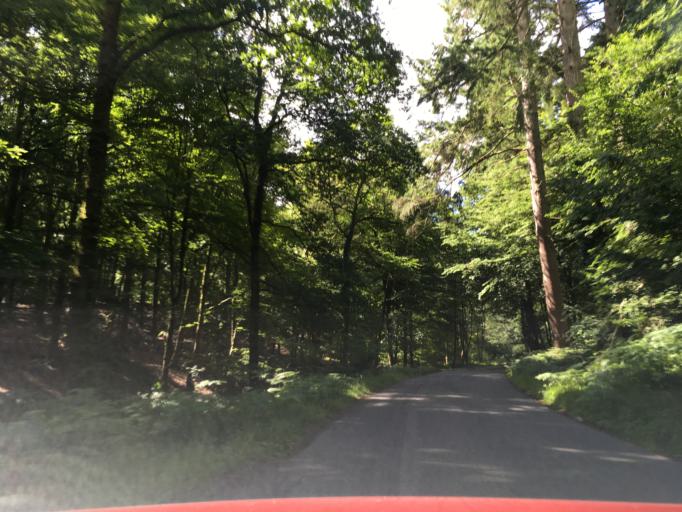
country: GB
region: England
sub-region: Gloucestershire
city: Cinderford
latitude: 51.7806
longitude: -2.5003
